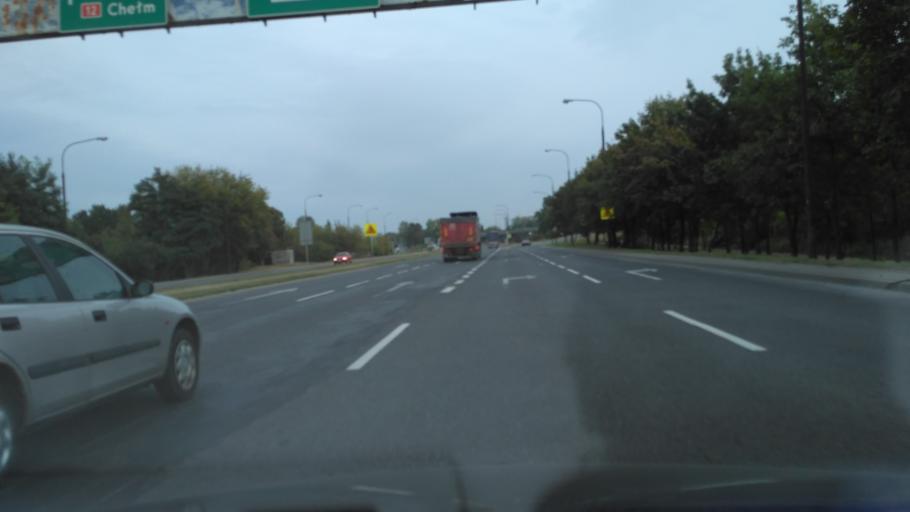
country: PL
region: Lublin Voivodeship
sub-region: Powiat lubelski
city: Lublin
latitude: 51.2504
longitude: 22.5819
